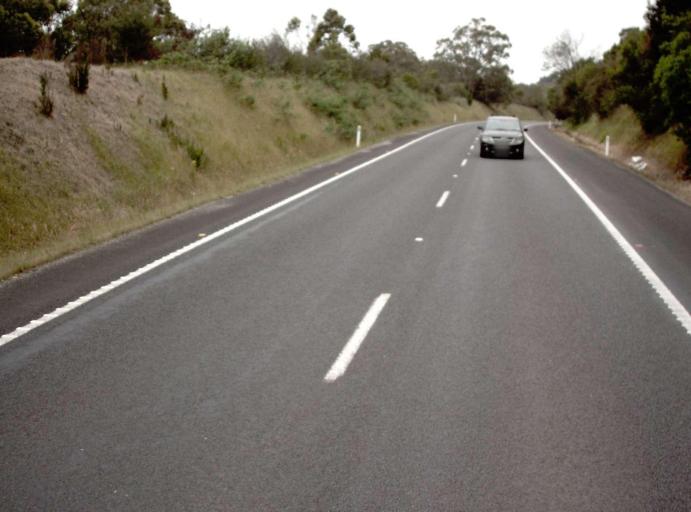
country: AU
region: Victoria
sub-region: Latrobe
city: Moe
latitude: -38.1965
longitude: 146.2873
